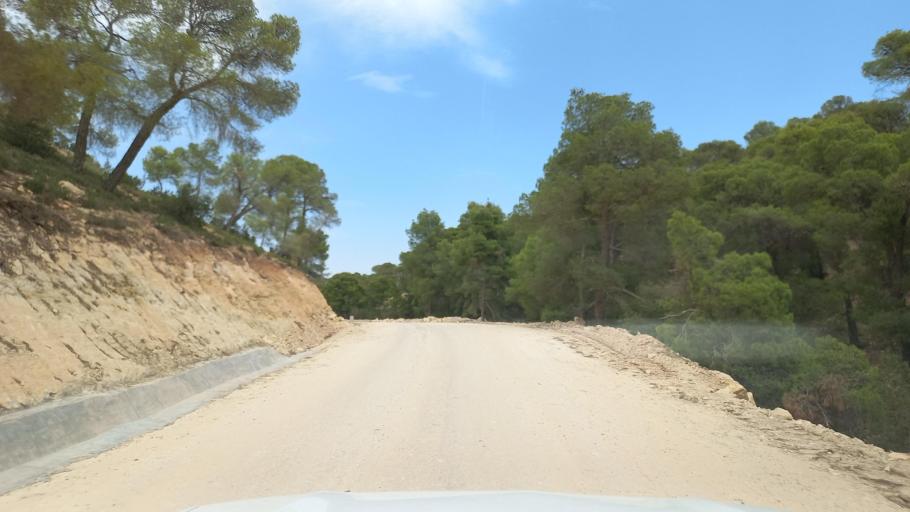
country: TN
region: Al Qasrayn
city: Kasserine
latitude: 35.3794
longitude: 8.8821
